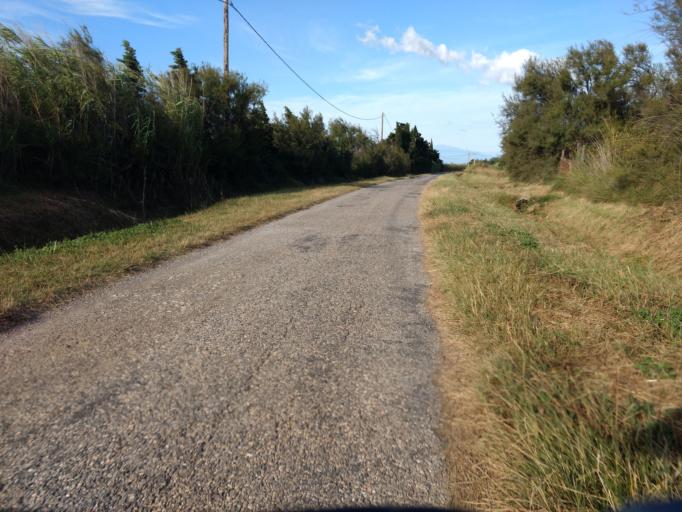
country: FR
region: Languedoc-Roussillon
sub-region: Departement des Pyrenees-Orientales
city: Saint-Laurent-de-la-Salanque
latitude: 42.7846
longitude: 3.0087
